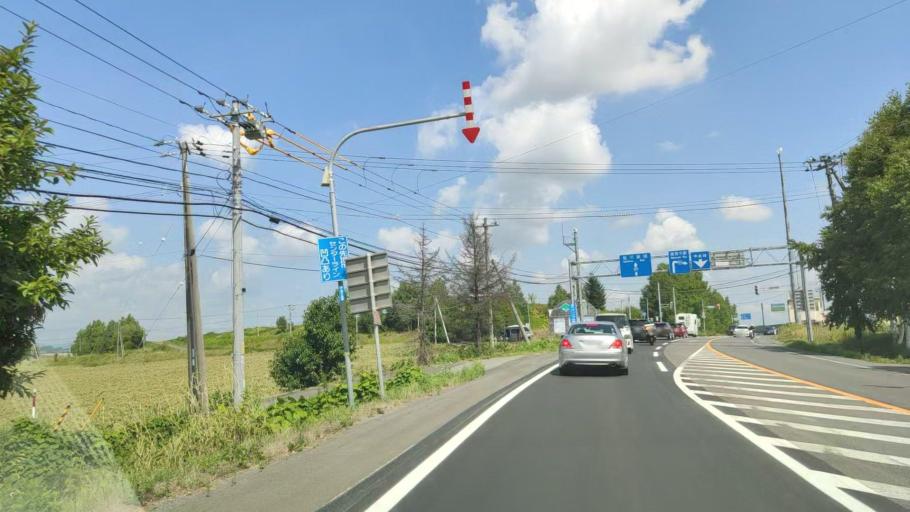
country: JP
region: Hokkaido
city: Shimo-furano
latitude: 43.5445
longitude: 142.4385
